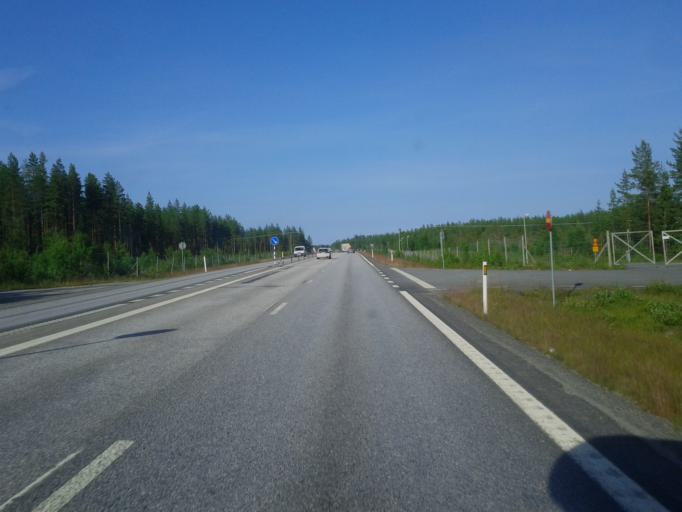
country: SE
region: Vaesterbotten
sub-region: Umea Kommun
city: Saevar
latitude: 63.8848
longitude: 20.5002
